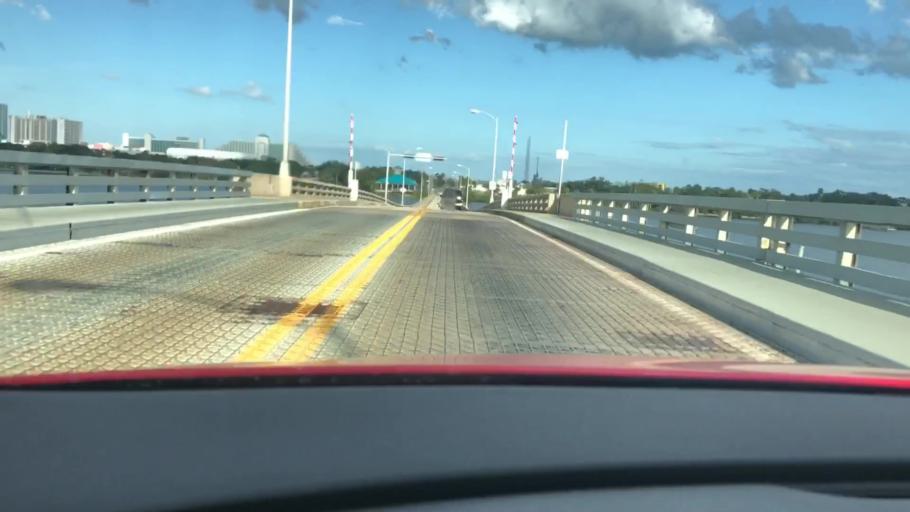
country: US
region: Florida
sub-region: Volusia County
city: Daytona Beach
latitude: 29.2227
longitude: -81.0201
